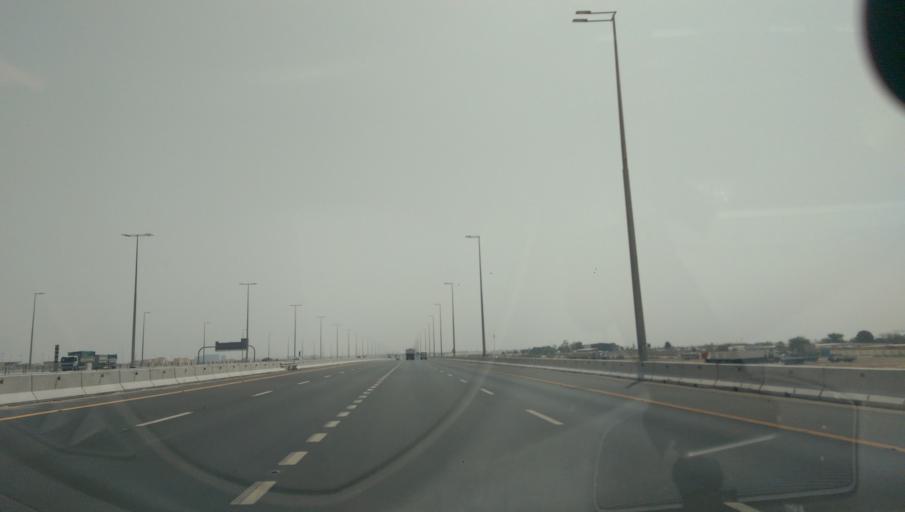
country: AE
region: Abu Dhabi
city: Abu Dhabi
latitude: 24.2919
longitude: 54.5658
